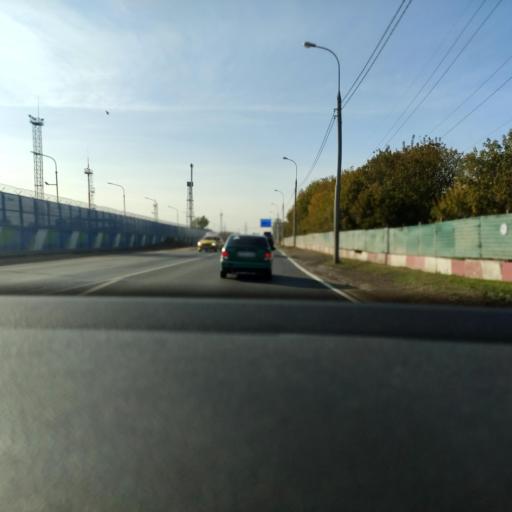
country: RU
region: Moscow
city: Kapotnya
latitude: 55.6568
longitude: 37.8096
